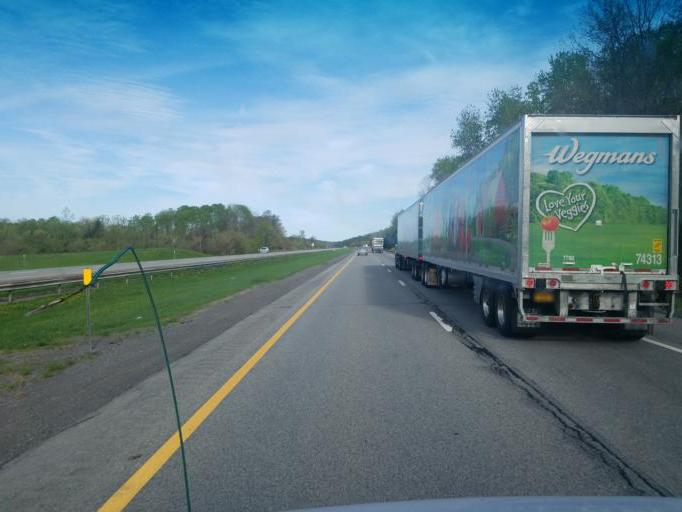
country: US
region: New York
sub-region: Herkimer County
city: Little Falls
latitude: 43.0106
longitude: -74.9150
